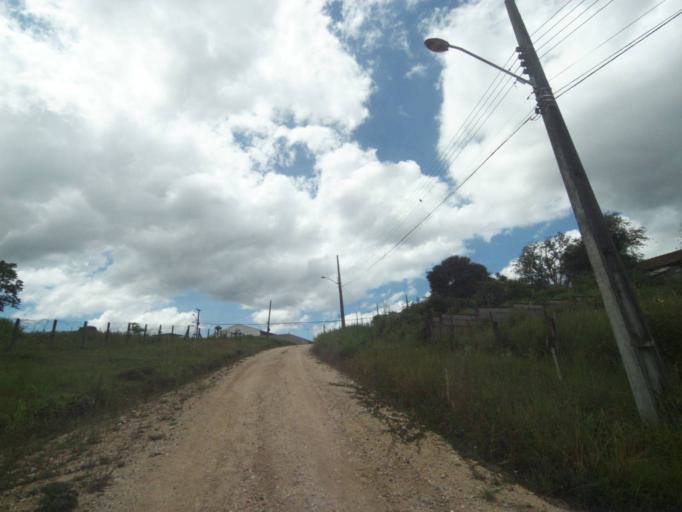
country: BR
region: Parana
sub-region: Curitiba
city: Curitiba
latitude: -25.4332
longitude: -49.3201
